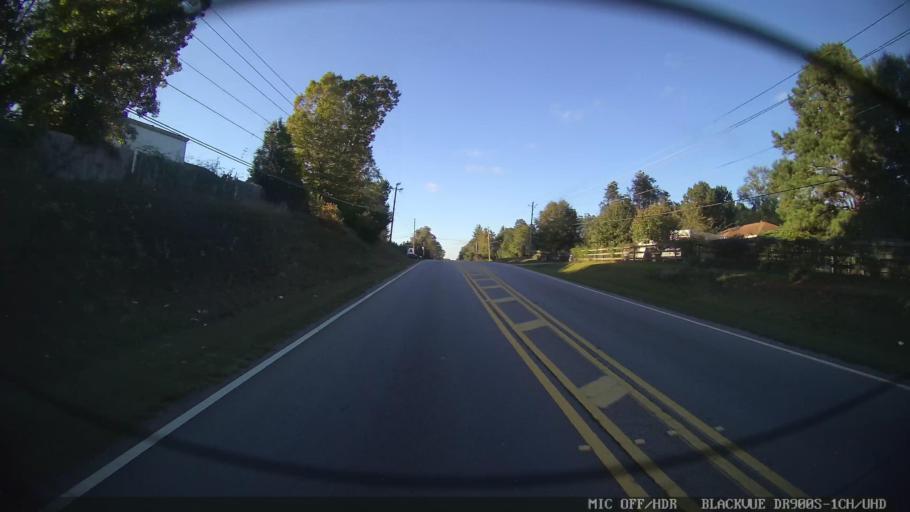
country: US
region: Georgia
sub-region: Clayton County
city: Lake City
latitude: 33.5999
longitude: -84.2983
